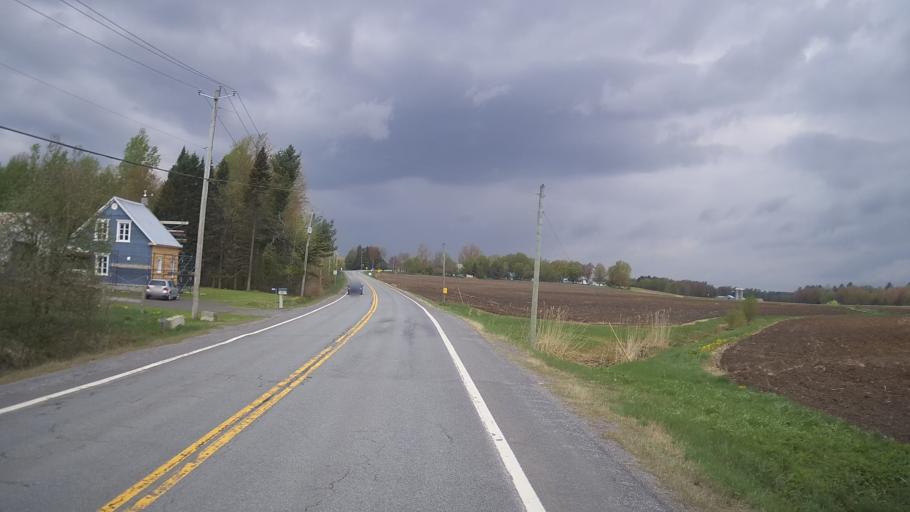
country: CA
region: Quebec
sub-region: Monteregie
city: Farnham
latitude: 45.2424
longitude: -72.8846
